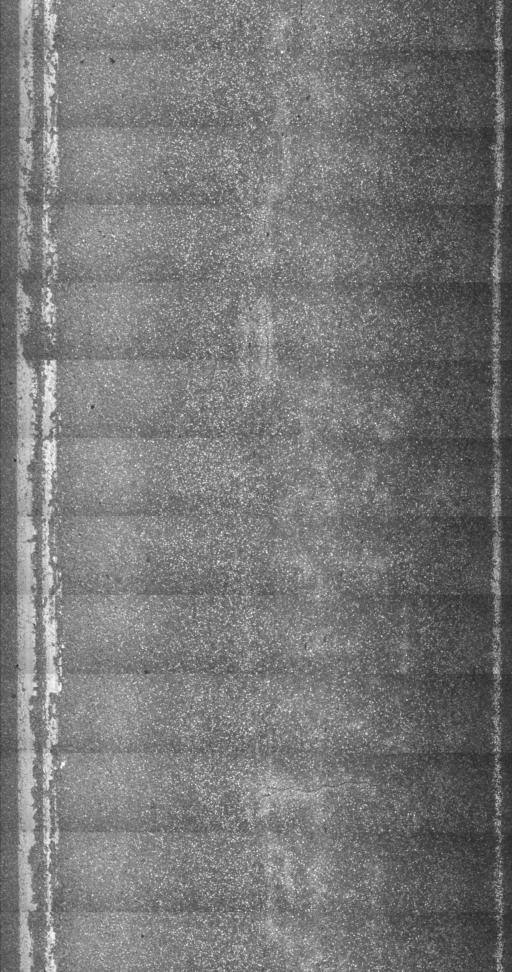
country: US
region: Vermont
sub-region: Chittenden County
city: Essex Junction
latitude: 44.4816
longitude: -73.1154
